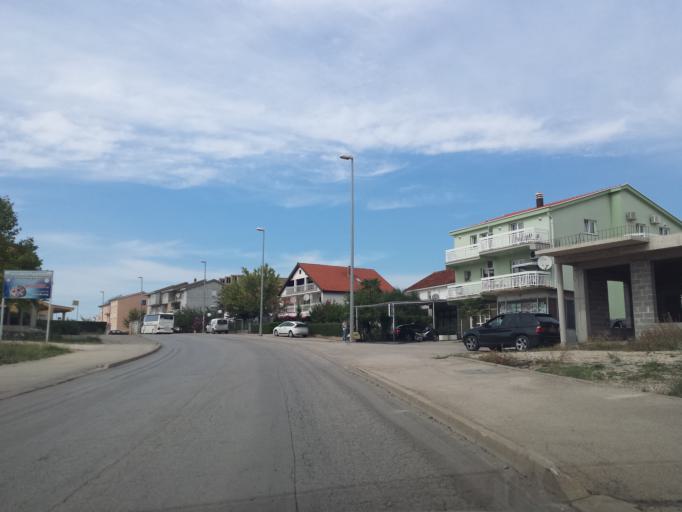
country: BA
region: Federation of Bosnia and Herzegovina
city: Citluk
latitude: 43.1998
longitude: 17.6720
